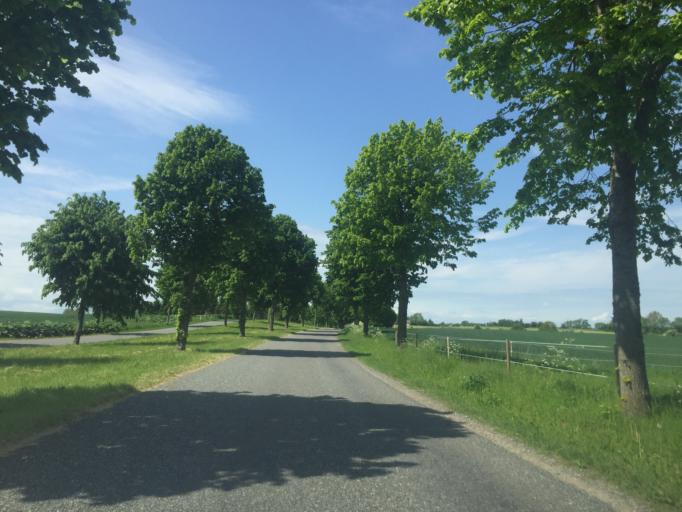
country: DK
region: South Denmark
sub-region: Svendborg Kommune
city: Thuro By
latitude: 55.1395
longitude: 10.7250
